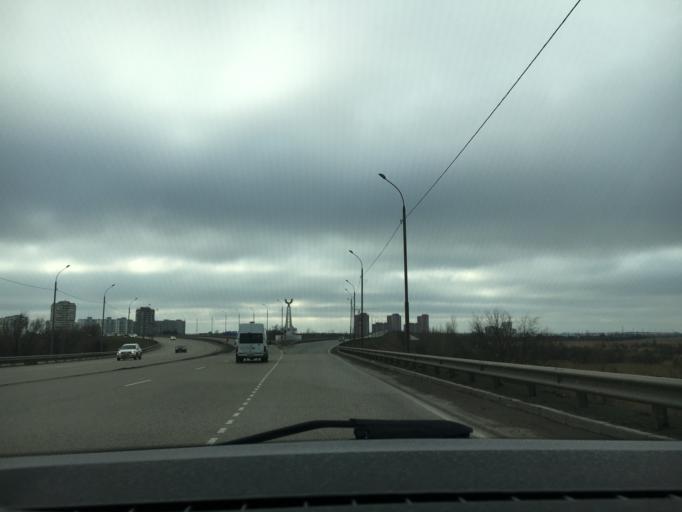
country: RU
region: Rostov
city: Bataysk
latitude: 47.1645
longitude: 39.7421
